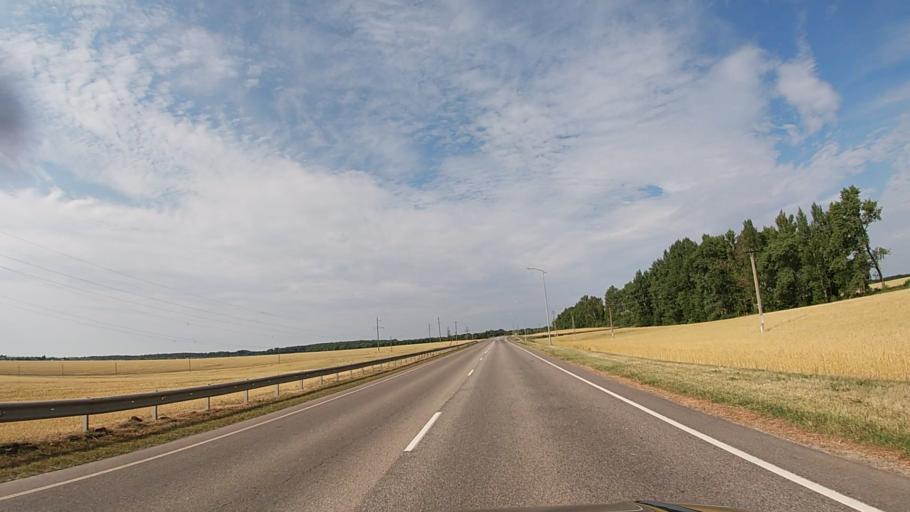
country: RU
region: Belgorod
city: Proletarskiy
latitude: 50.8100
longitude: 35.7466
